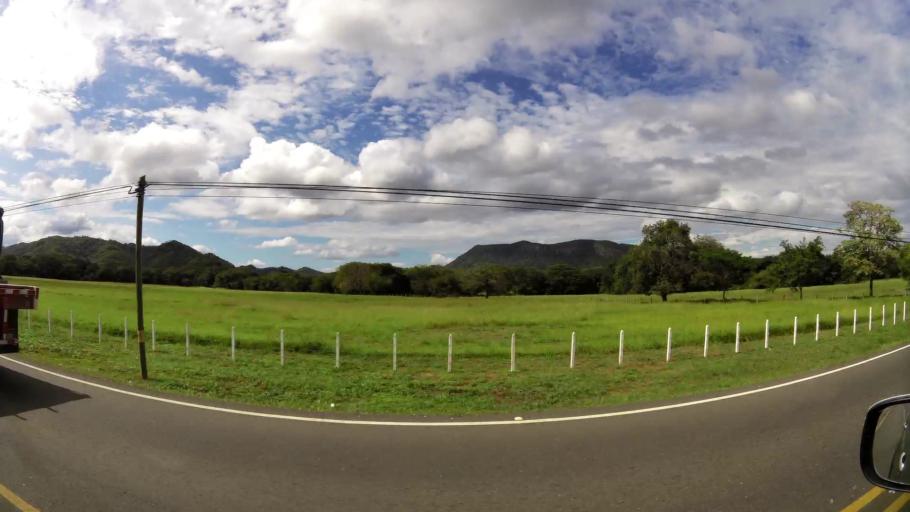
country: CR
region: Guanacaste
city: Hojancha
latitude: 10.1338
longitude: -85.3401
